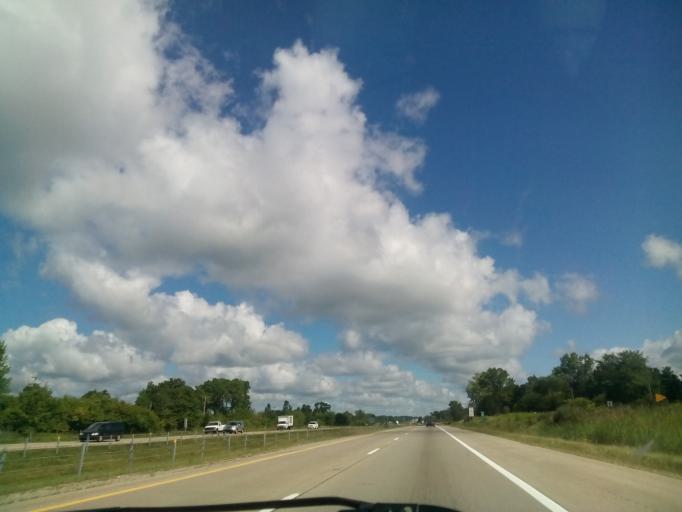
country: US
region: Michigan
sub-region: Genesee County
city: Fenton
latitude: 42.6849
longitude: -83.7601
